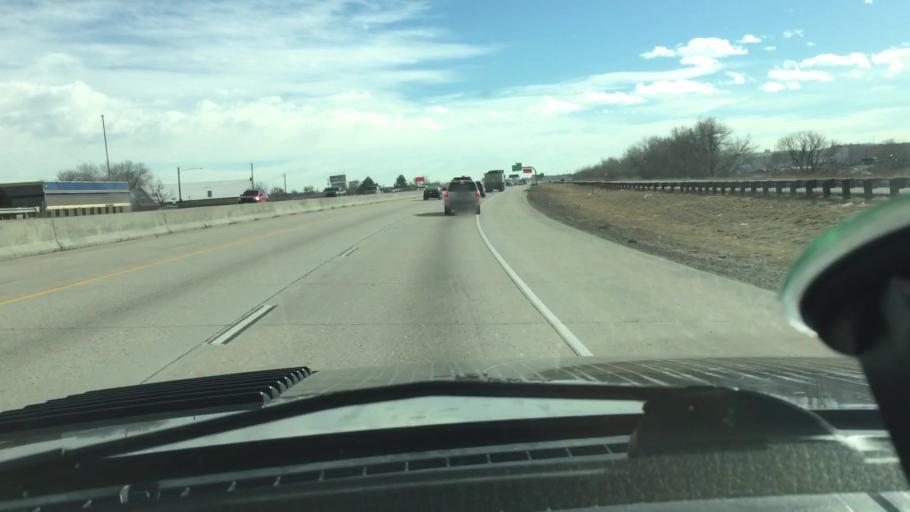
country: US
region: Colorado
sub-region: Adams County
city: Commerce City
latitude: 39.7935
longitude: -104.9142
